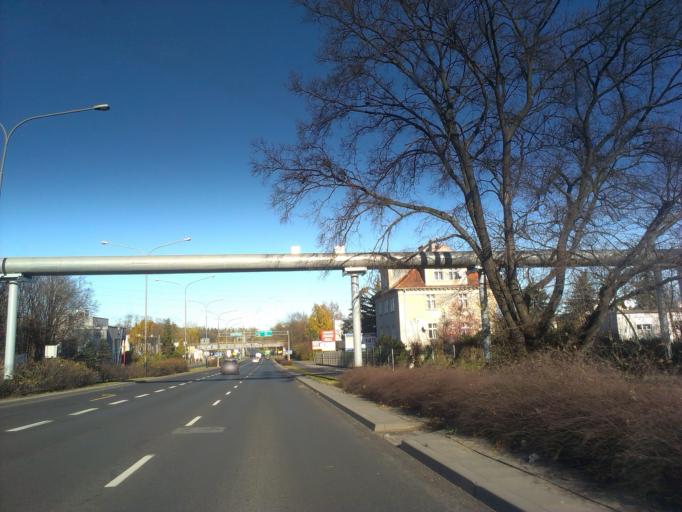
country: PL
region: Greater Poland Voivodeship
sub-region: Poznan
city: Poznan
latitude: 52.4177
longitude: 16.8929
